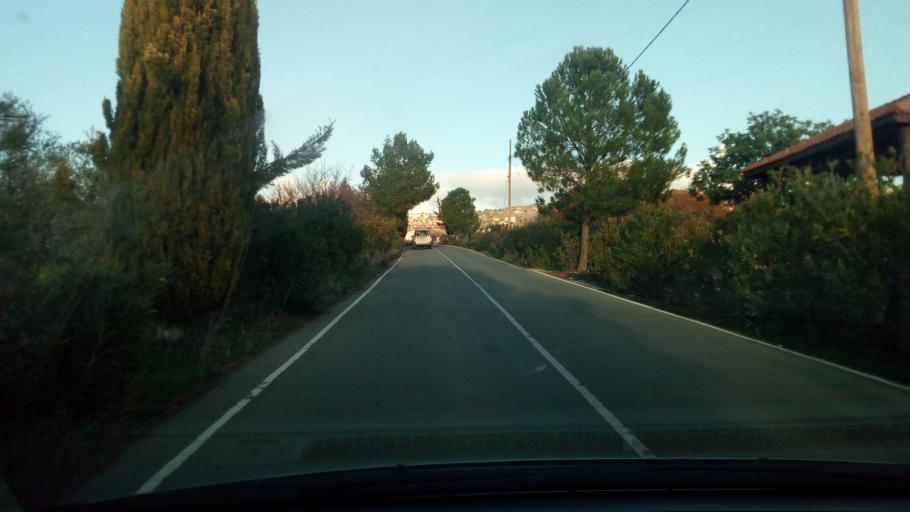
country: CY
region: Pafos
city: Polis
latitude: 34.9846
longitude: 32.4701
